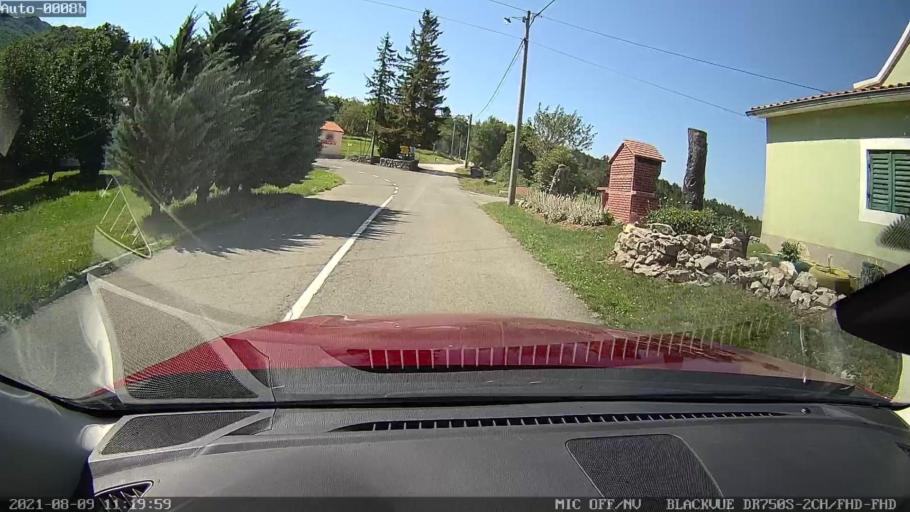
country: HR
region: Istarska
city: Lovran
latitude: 45.3047
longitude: 14.1935
